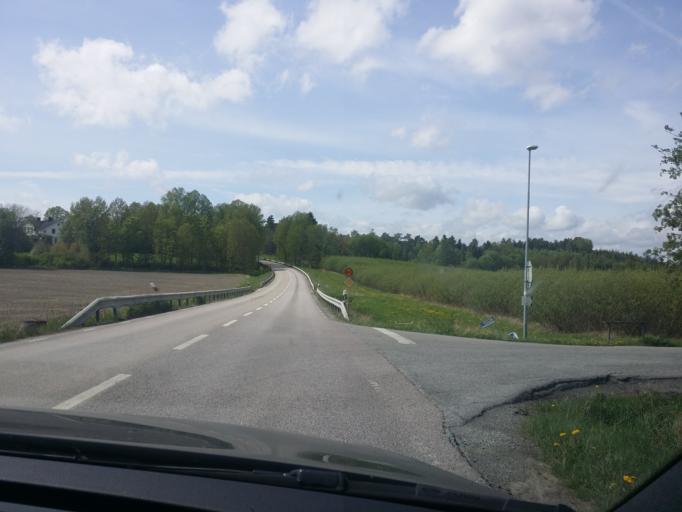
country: SE
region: Stockholm
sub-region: Sigtuna Kommun
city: Sigtuna
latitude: 59.6493
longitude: 17.6414
